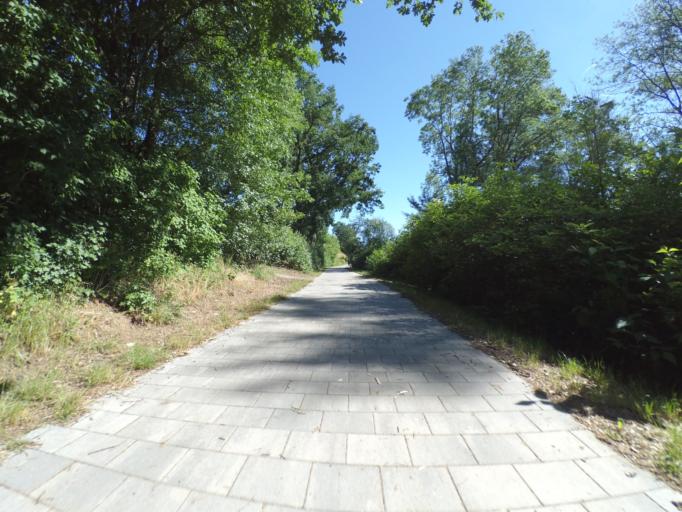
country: DE
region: Mecklenburg-Vorpommern
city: Plau am See
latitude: 53.4685
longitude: 12.2838
